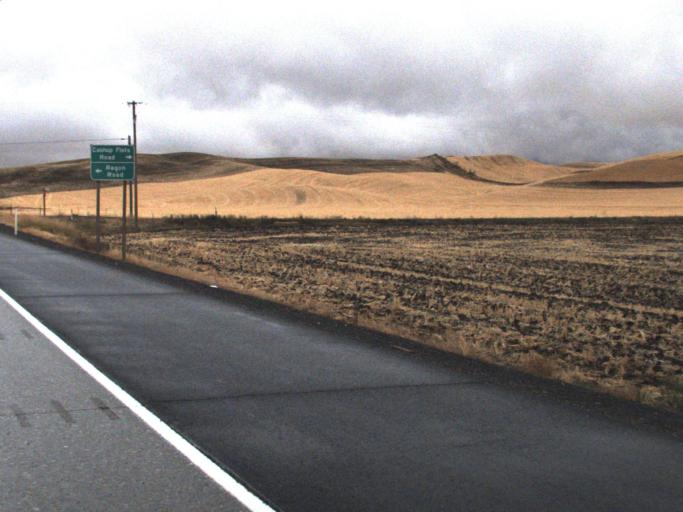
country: US
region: Washington
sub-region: Whitman County
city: Colfax
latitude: 47.0589
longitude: -117.3812
